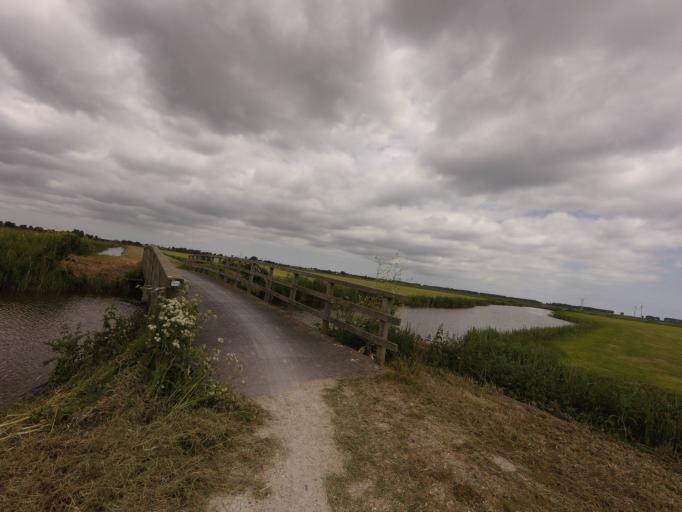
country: NL
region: North Holland
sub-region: Gemeente Beemster
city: Halfweg
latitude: 52.6064
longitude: 4.9727
